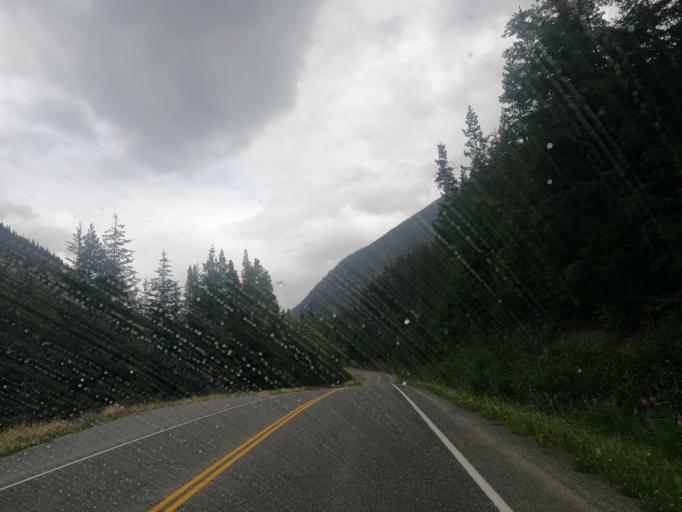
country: CA
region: British Columbia
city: Lillooet
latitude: 50.4905
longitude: -122.2000
